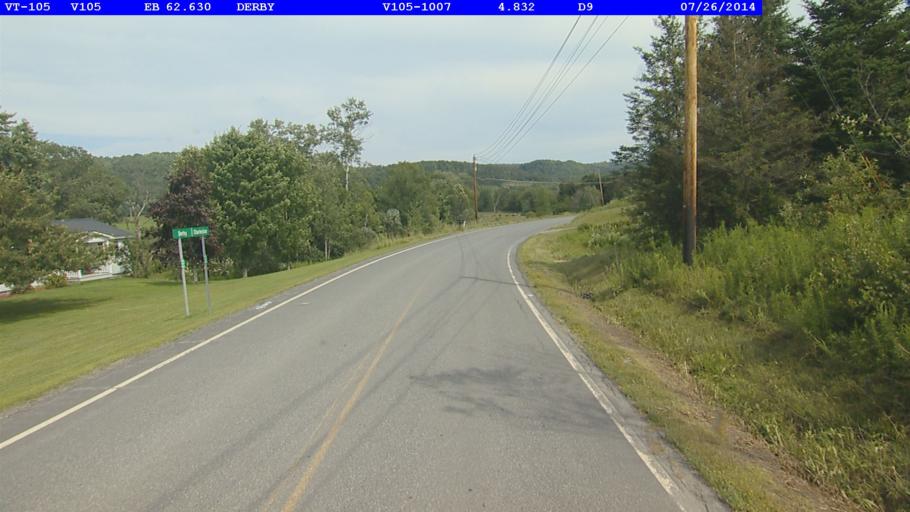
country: US
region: Vermont
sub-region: Orleans County
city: Newport
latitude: 44.9053
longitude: -72.0768
